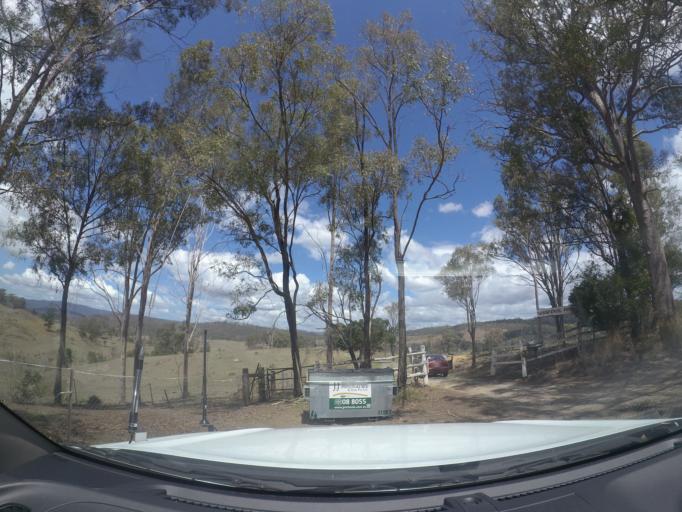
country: AU
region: Queensland
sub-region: Logan
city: Cedar Vale
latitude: -27.9009
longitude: 153.0461
